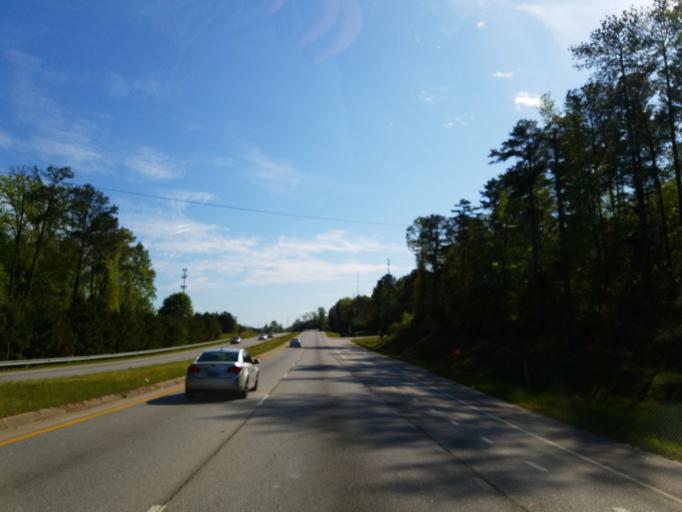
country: US
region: Georgia
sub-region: Douglas County
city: Lithia Springs
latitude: 33.7171
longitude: -84.6610
